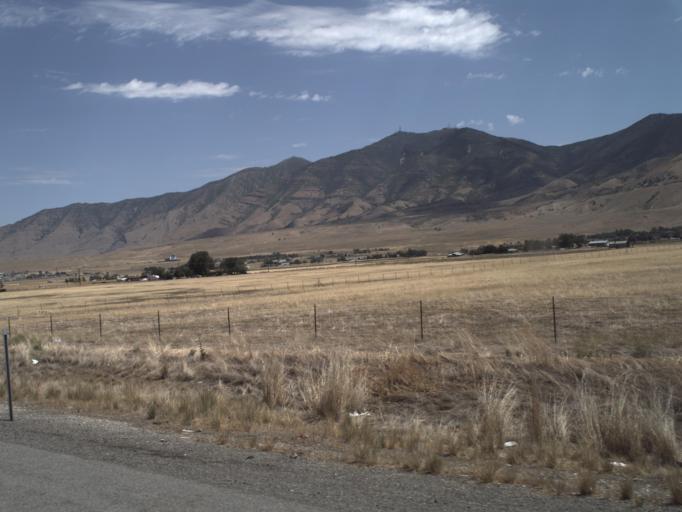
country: US
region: Utah
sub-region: Tooele County
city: Erda
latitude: 40.5944
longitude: -112.2940
